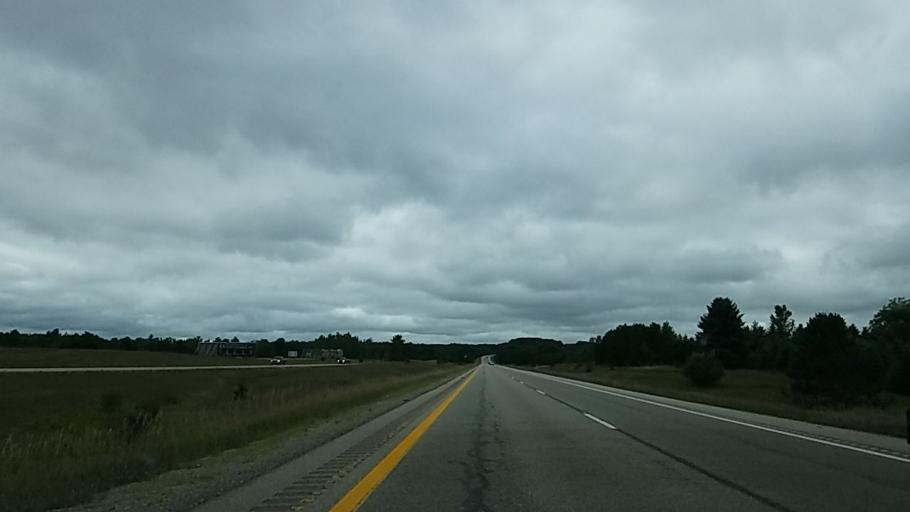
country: US
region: Michigan
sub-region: Otsego County
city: Gaylord
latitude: 45.1357
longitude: -84.6713
